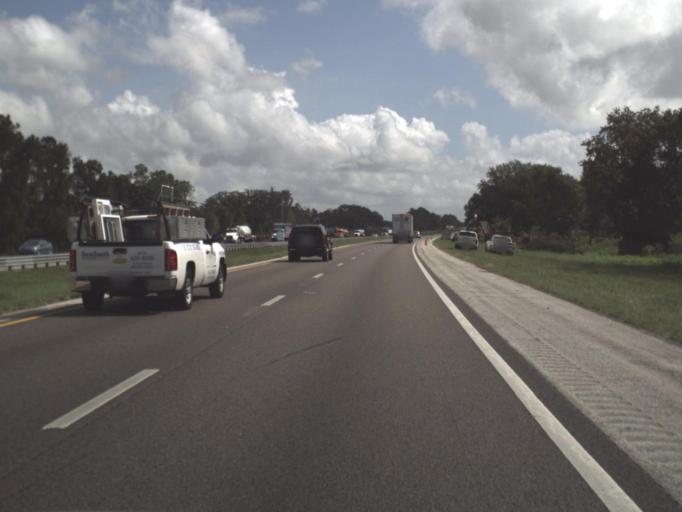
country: US
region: Florida
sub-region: Pasco County
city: Wesley Chapel
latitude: 28.2540
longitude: -82.3413
